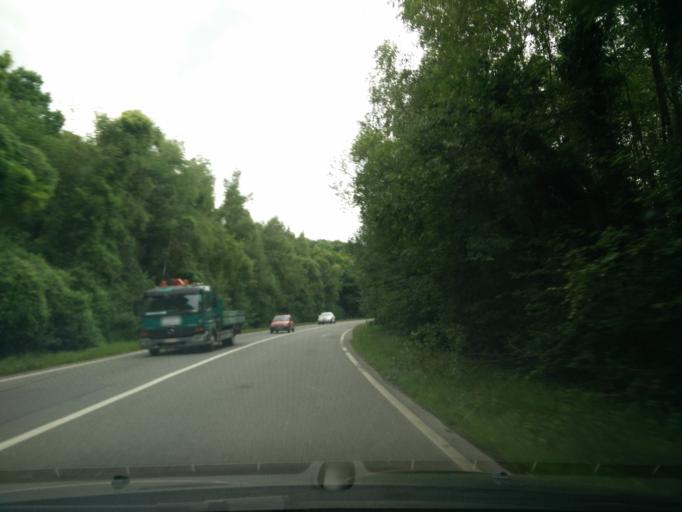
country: BE
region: Wallonia
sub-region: Province de Liege
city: Oupeye
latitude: 50.7534
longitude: 5.6575
